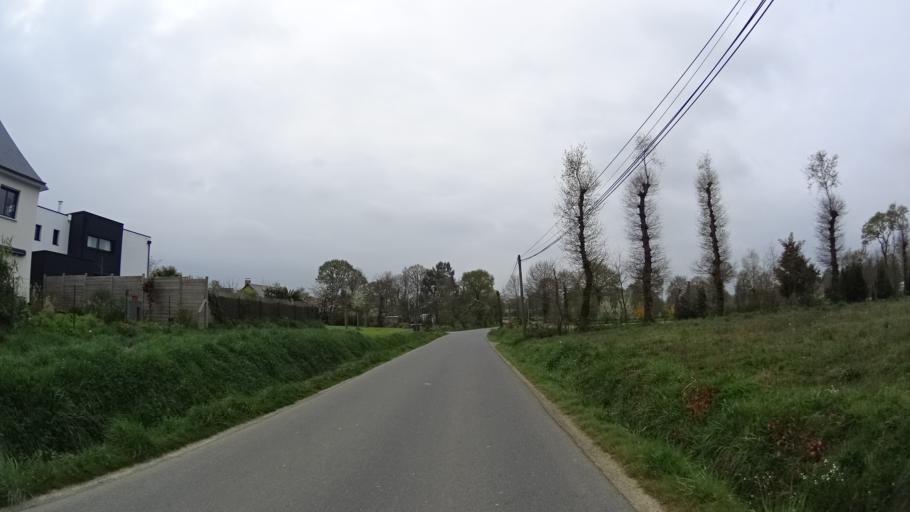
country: FR
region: Brittany
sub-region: Departement d'Ille-et-Vilaine
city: Saint-Gilles
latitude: 48.1524
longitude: -1.8419
